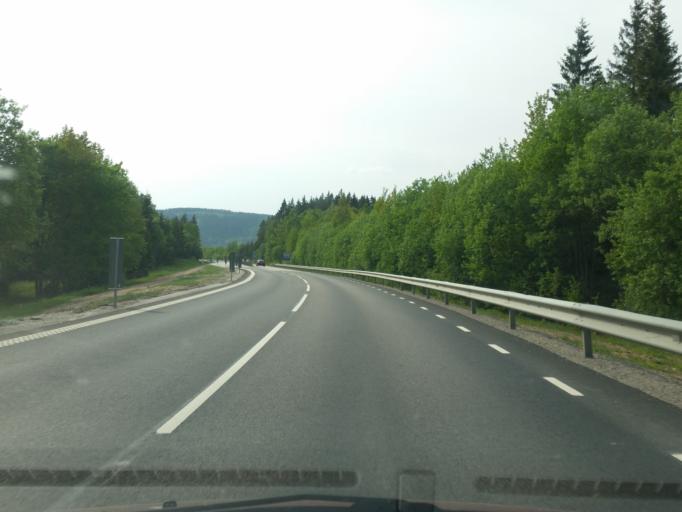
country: SE
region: Vaestra Goetaland
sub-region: Ulricehamns Kommun
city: Ulricehamn
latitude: 57.8085
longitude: 13.4500
